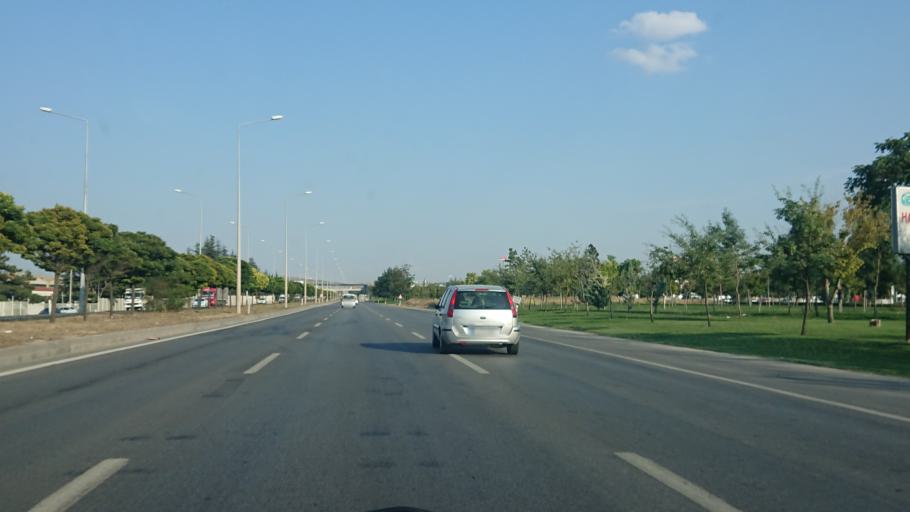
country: TR
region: Eskisehir
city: Sevinc
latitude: 39.7448
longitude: 30.6144
